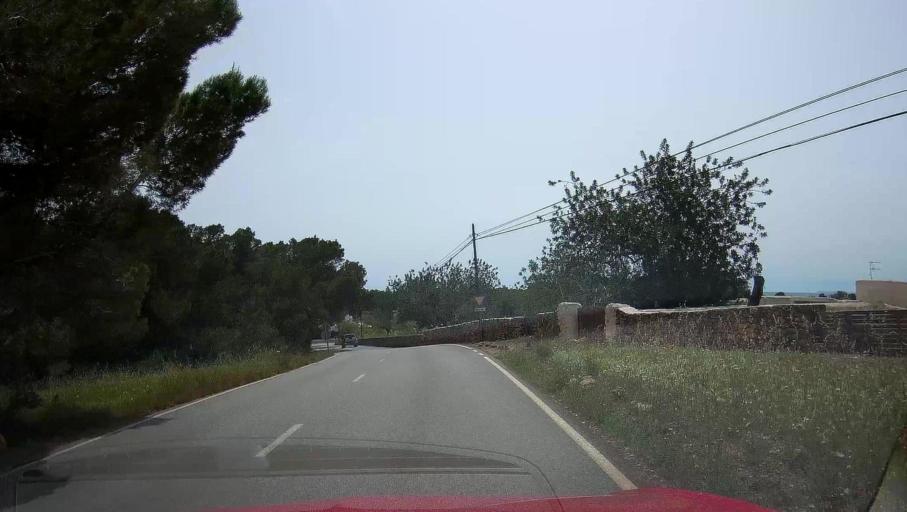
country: ES
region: Balearic Islands
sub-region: Illes Balears
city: Santa Eularia des Riu
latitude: 39.0059
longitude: 1.5703
